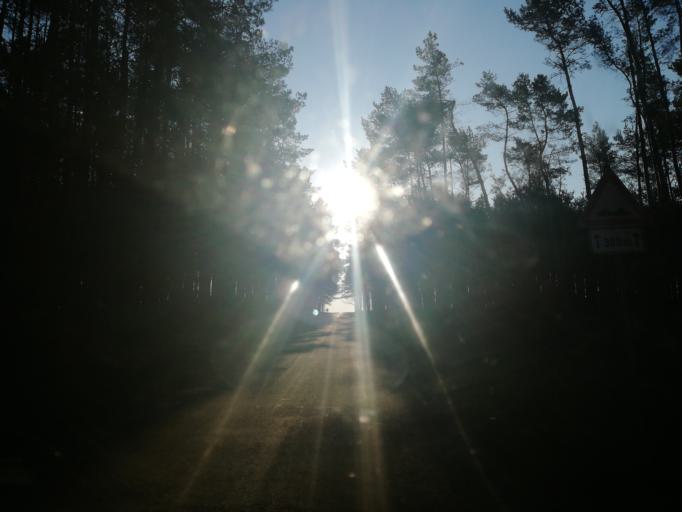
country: DE
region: Brandenburg
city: Drahnsdorf
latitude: 51.8926
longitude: 13.5859
